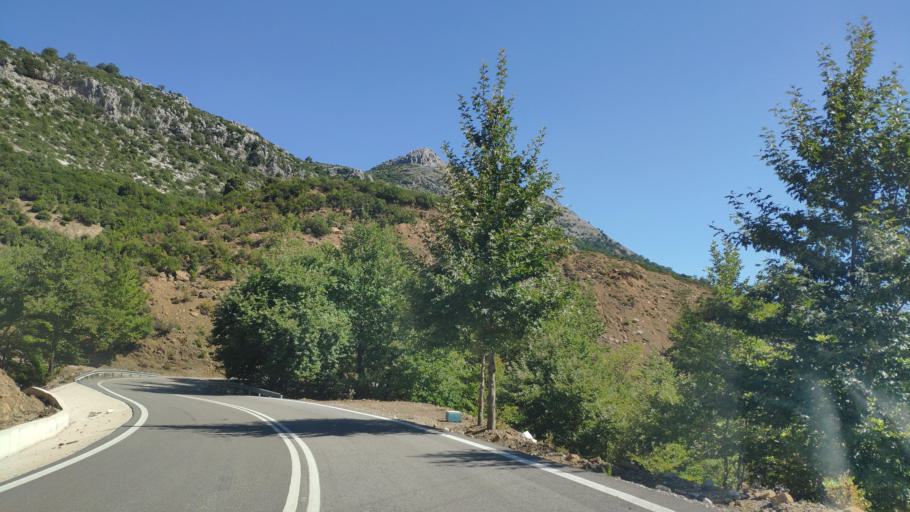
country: GR
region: Central Greece
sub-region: Nomos Evrytanias
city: Kerasochori
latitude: 38.9263
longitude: 21.4288
